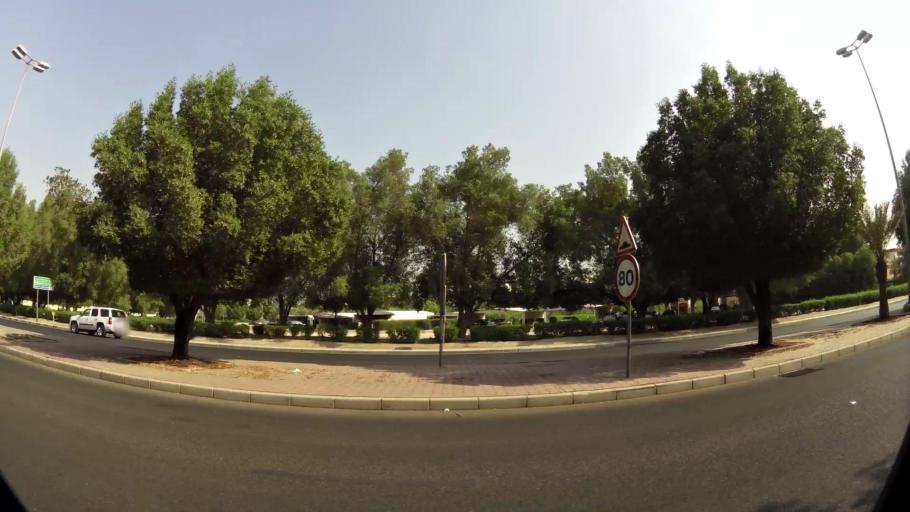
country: KW
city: Bayan
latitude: 29.2972
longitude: 48.0505
